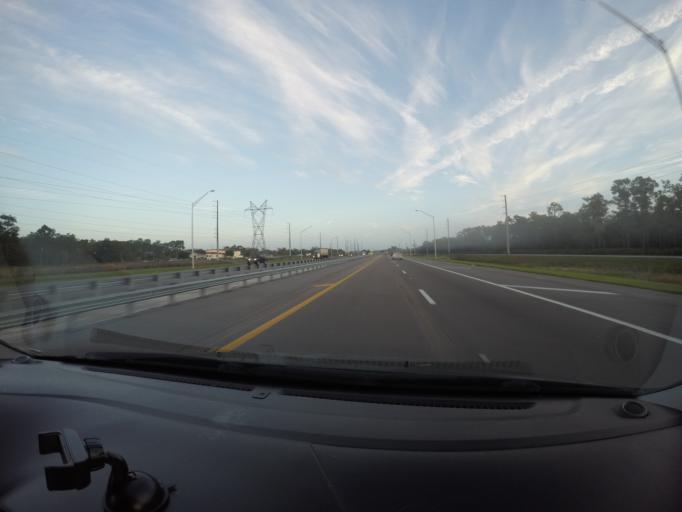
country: US
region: Florida
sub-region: Orange County
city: Azalea Park
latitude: 28.5297
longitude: -81.2508
